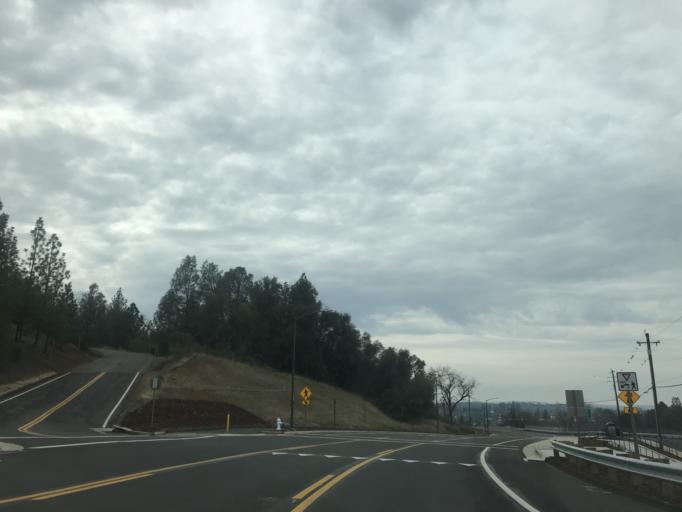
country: US
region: California
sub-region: El Dorado County
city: Placerville
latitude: 38.7259
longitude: -120.8241
